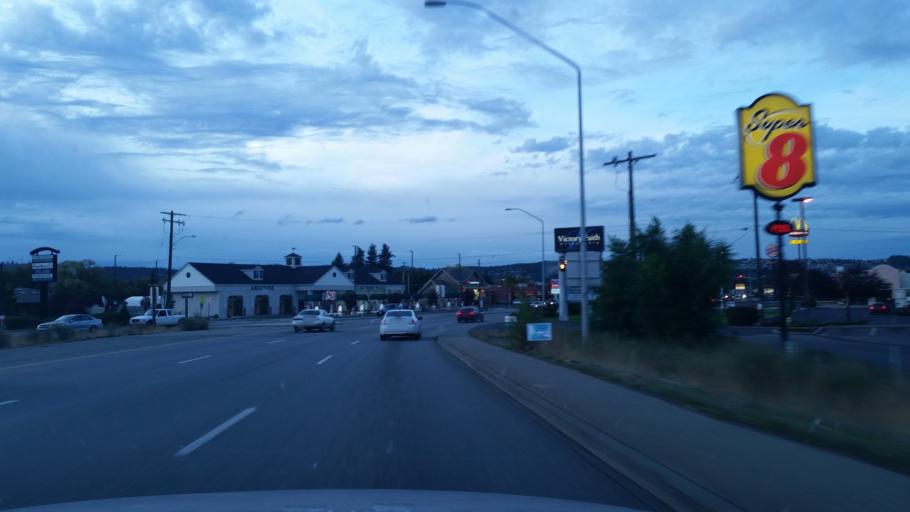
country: US
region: Washington
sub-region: Spokane County
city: Millwood
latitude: 47.6750
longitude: -117.2821
